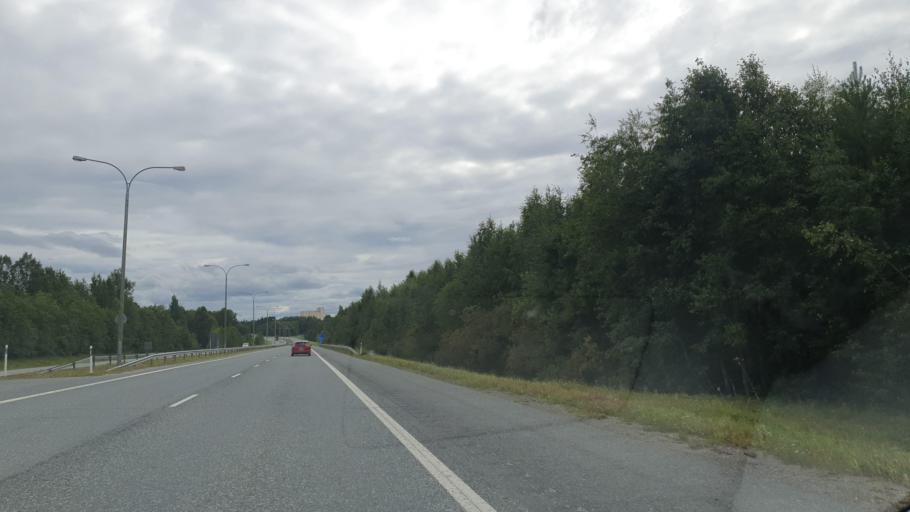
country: FI
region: Northern Savo
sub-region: Ylae-Savo
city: Iisalmi
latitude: 63.5370
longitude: 27.2470
